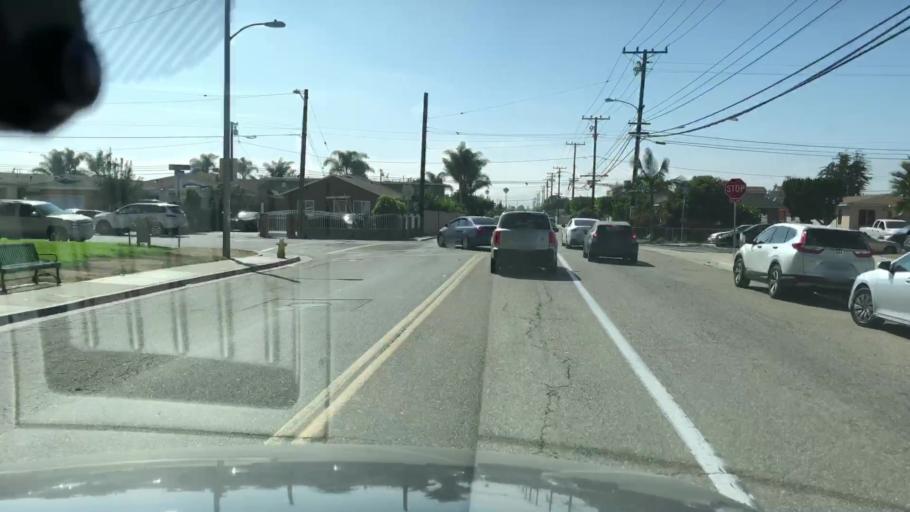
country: US
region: California
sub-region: Ventura County
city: Oxnard
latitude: 34.2064
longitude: -119.1680
